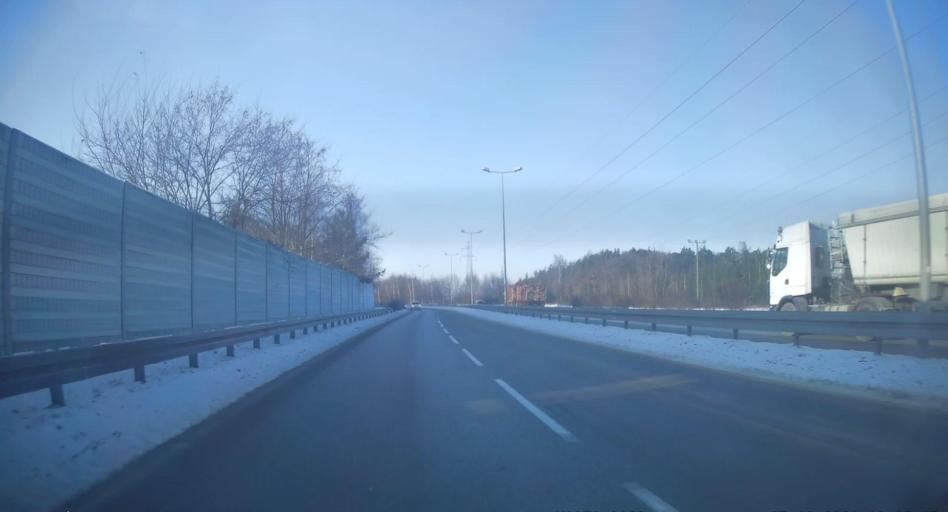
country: PL
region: Lodz Voivodeship
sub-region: Piotrkow Trybunalski
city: Piotrkow Trybunalski
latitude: 51.4203
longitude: 19.7180
